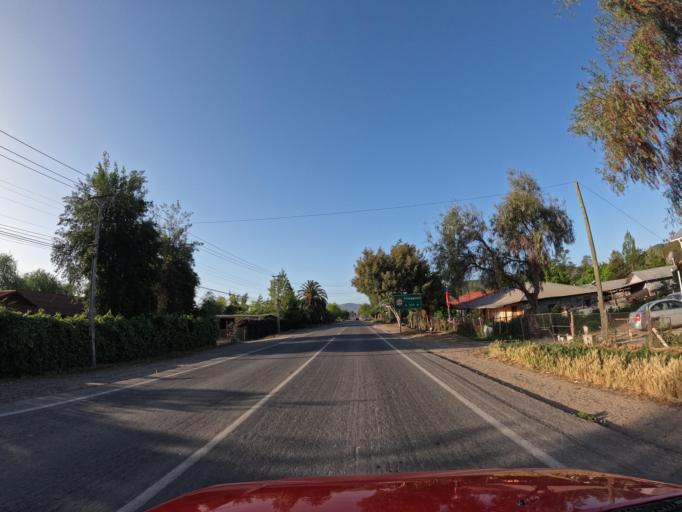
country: CL
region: O'Higgins
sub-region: Provincia de Colchagua
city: Santa Cruz
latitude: -34.4219
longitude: -71.3739
